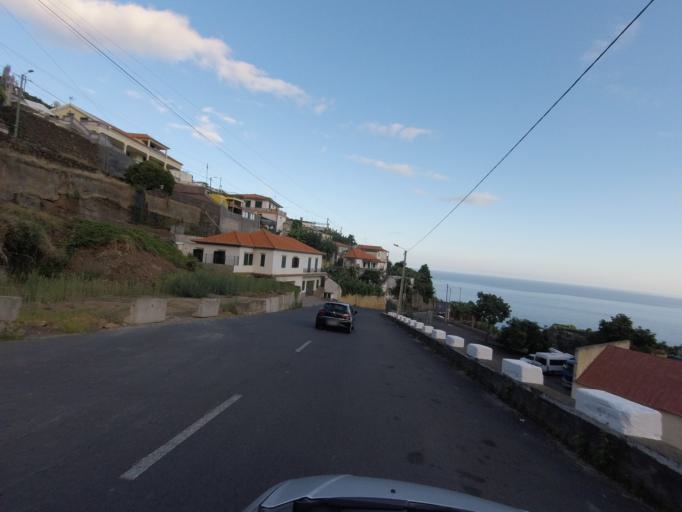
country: PT
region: Madeira
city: Ponta do Sol
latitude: 32.6880
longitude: -17.1075
